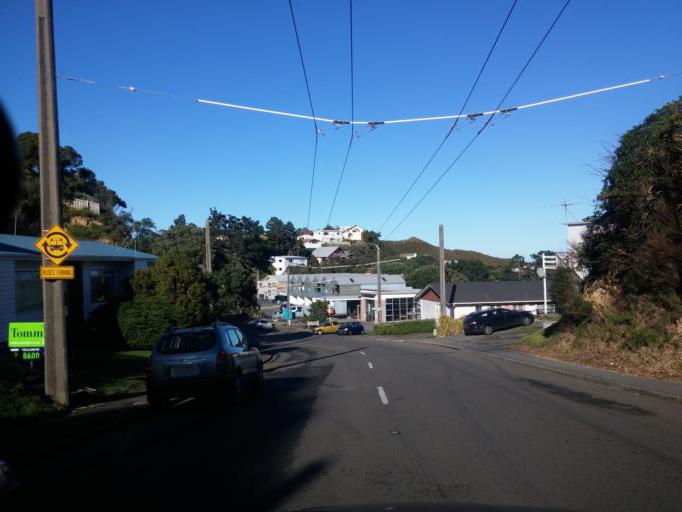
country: NZ
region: Wellington
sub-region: Wellington City
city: Brooklyn
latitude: -41.3223
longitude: 174.7631
